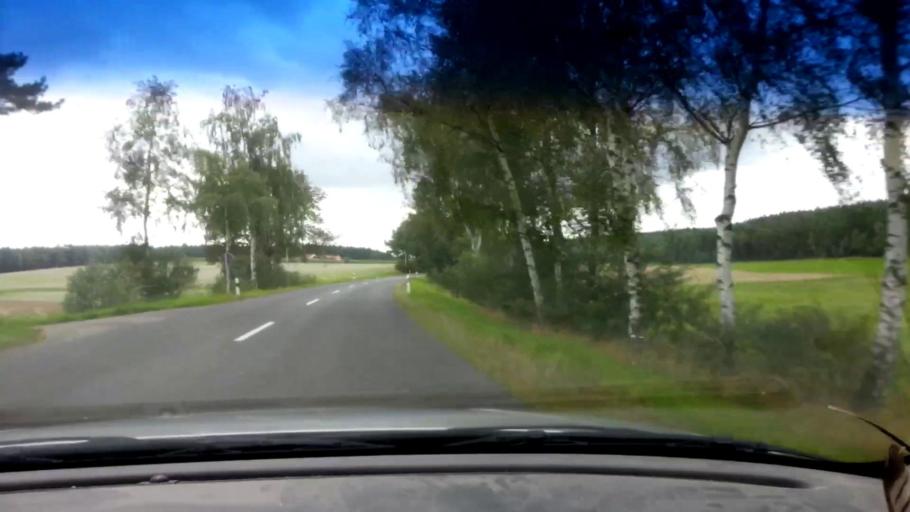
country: DE
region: Bavaria
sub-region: Upper Palatinate
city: Waldsassen
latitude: 50.0273
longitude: 12.3224
